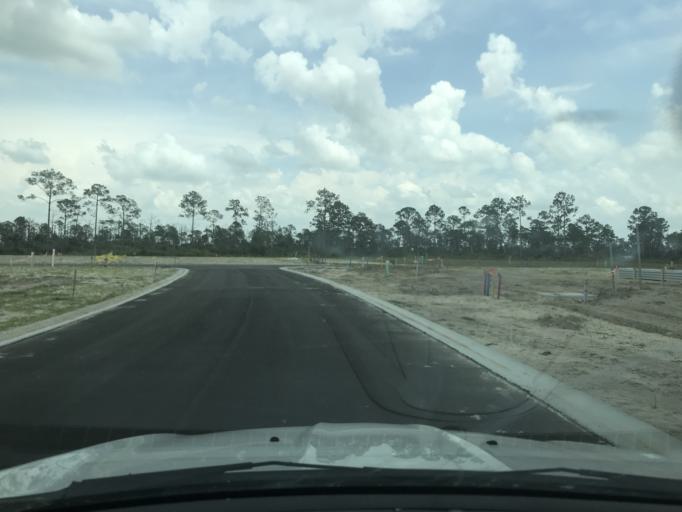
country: US
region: Florida
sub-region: Lee County
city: Olga
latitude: 26.7906
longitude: -81.7329
